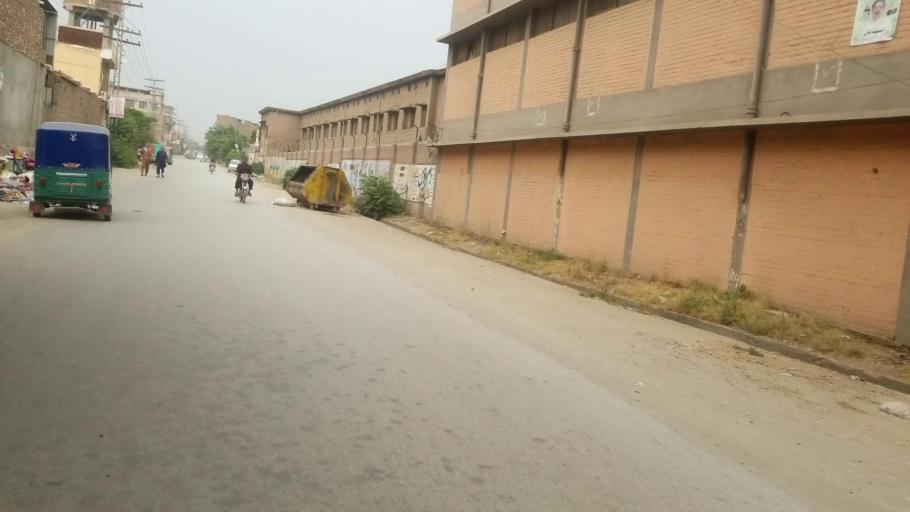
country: PK
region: Khyber Pakhtunkhwa
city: Peshawar
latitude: 33.9841
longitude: 71.5619
